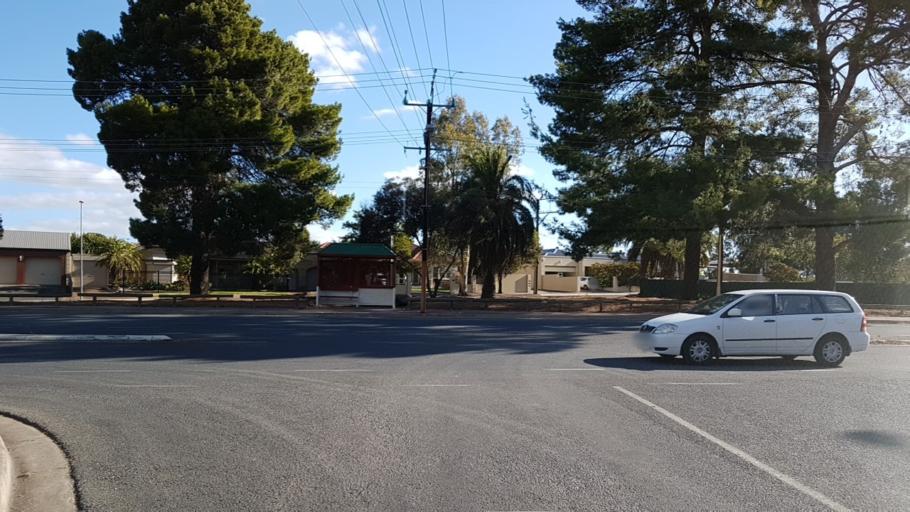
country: AU
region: South Australia
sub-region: Campbelltown
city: Athelstone
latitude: -34.8774
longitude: 138.6883
